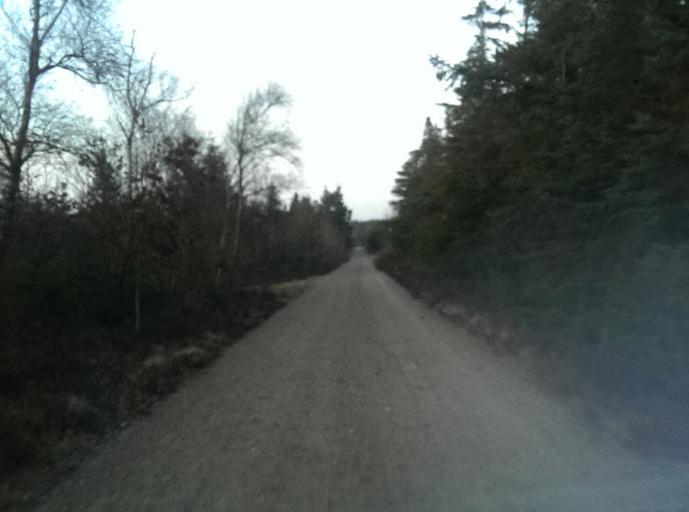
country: DK
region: South Denmark
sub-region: Varde Kommune
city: Oksbol
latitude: 55.5520
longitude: 8.3185
